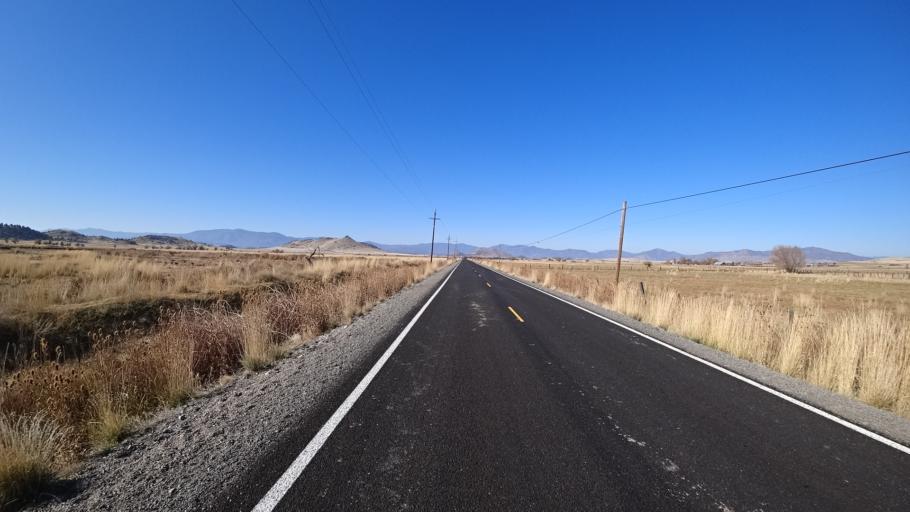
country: US
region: California
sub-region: Siskiyou County
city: Montague
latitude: 41.7114
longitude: -122.4269
